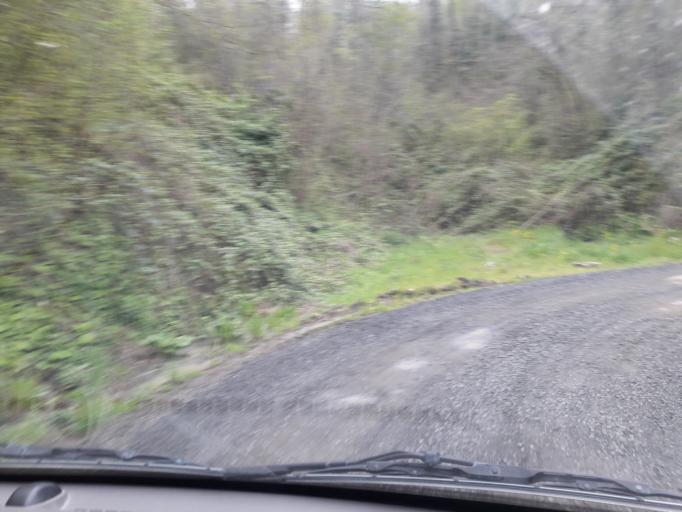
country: TR
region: Trabzon
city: Duzkoy
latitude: 40.9268
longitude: 39.4820
